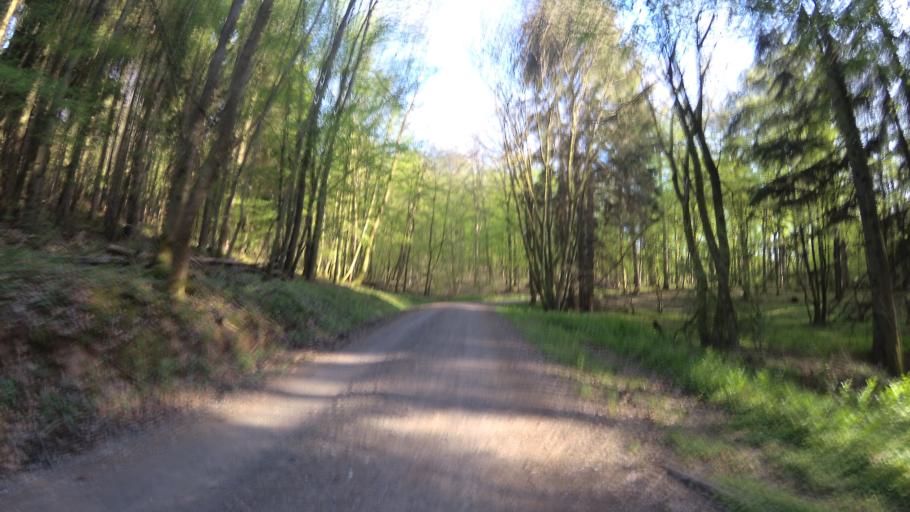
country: DE
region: Saarland
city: Mainzweiler
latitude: 49.4267
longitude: 7.1299
